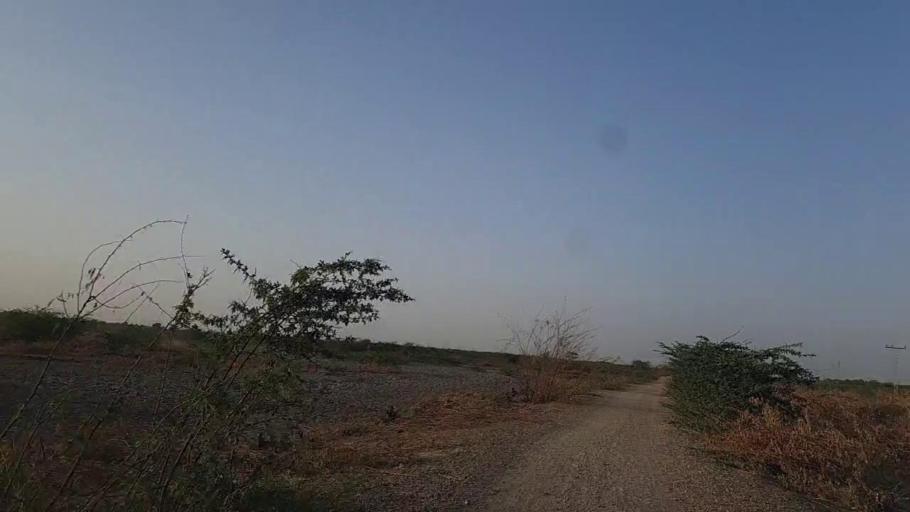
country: PK
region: Sindh
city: Naukot
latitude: 24.6435
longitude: 69.2520
